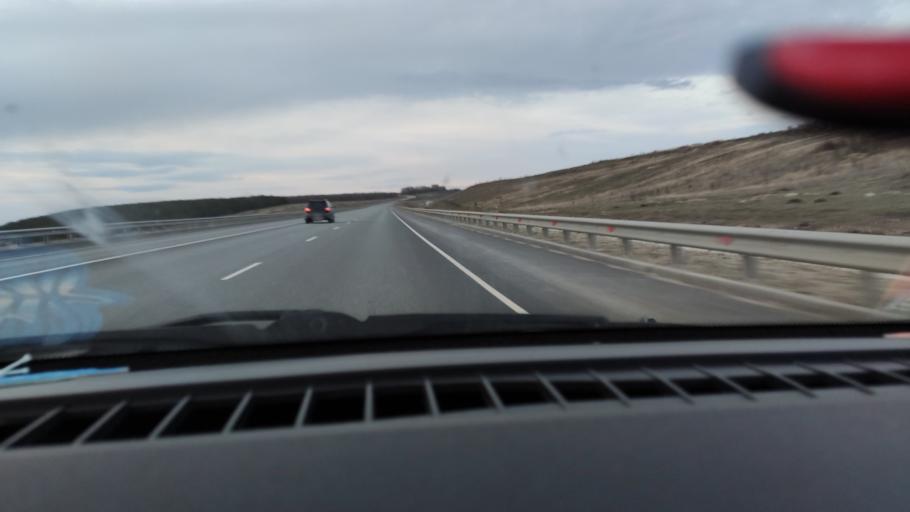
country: RU
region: Saratov
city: Yelshanka
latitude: 51.8789
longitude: 46.5087
